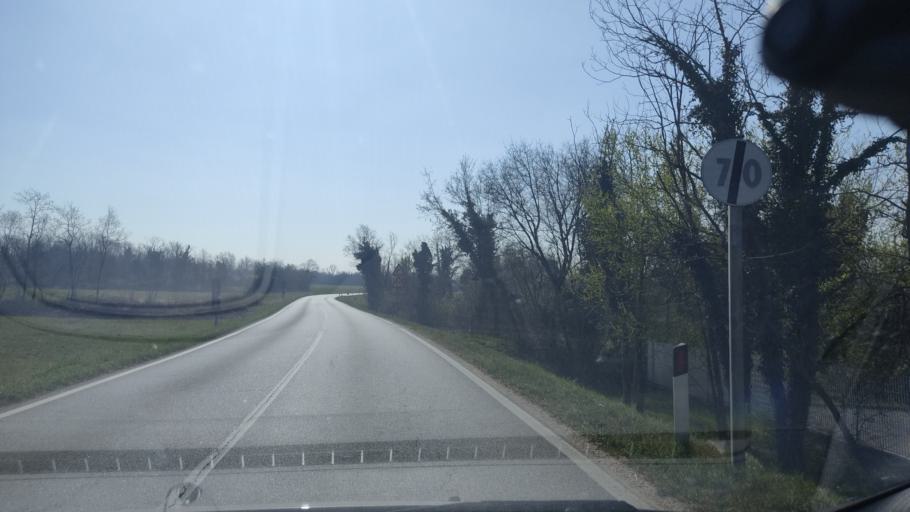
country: IT
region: Friuli Venezia Giulia
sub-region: Provincia di Pordenone
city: Budoia
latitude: 46.0351
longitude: 12.5489
